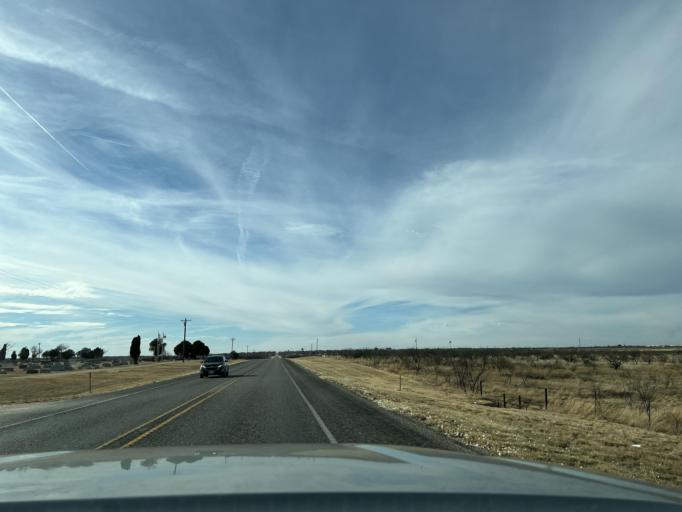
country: US
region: Texas
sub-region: Jones County
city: Anson
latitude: 32.7514
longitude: -99.8661
